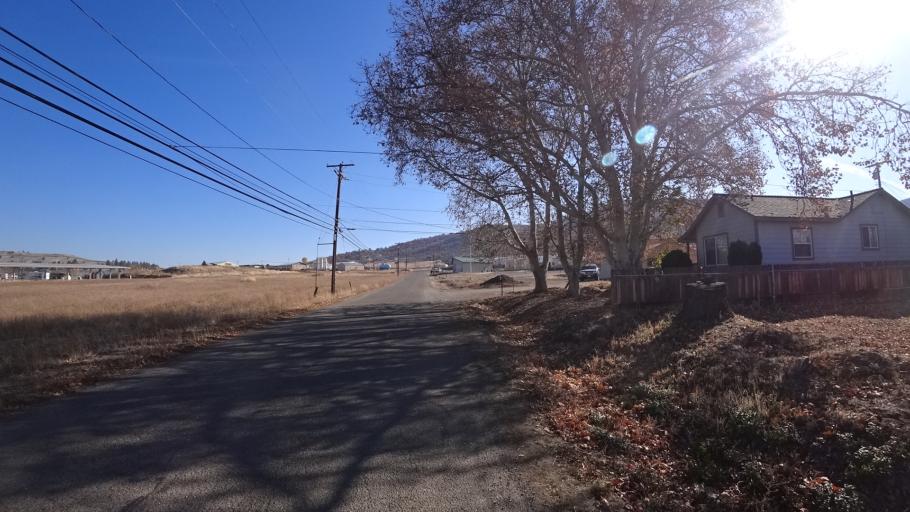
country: US
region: California
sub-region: Siskiyou County
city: Yreka
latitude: 41.7351
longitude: -122.6282
